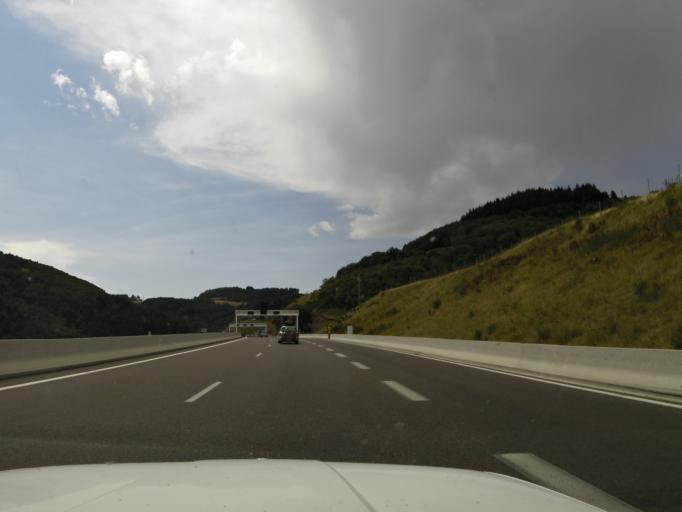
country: FR
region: Rhone-Alpes
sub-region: Departement de la Loire
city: Violay
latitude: 45.8661
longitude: 4.3877
